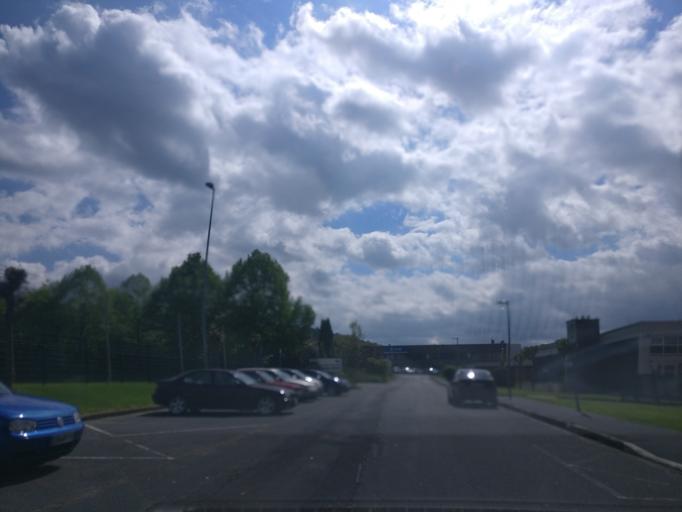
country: DE
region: Lower Saxony
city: Hannoversch Munden
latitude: 51.4332
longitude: 9.6470
